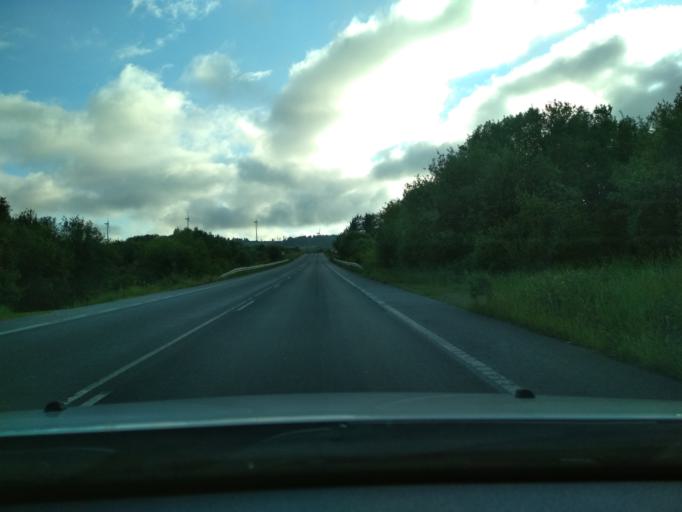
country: ES
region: Galicia
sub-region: Provincia da Coruna
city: Mazaricos
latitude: 42.9397
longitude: -8.9417
